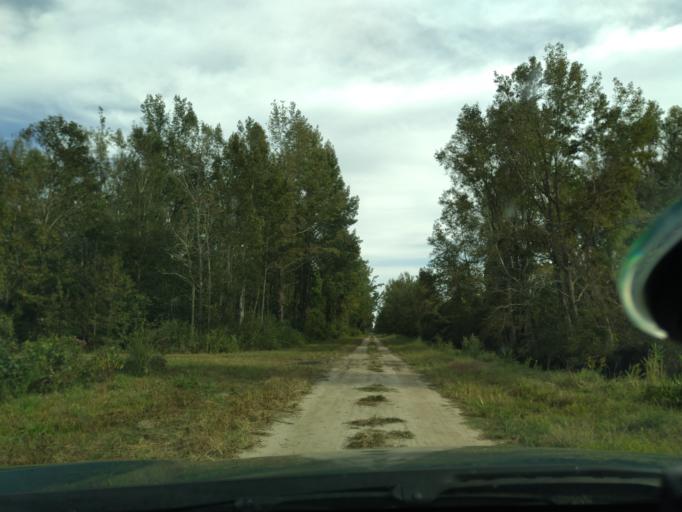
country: US
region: North Carolina
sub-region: Beaufort County
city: Belhaven
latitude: 35.7059
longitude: -76.5727
